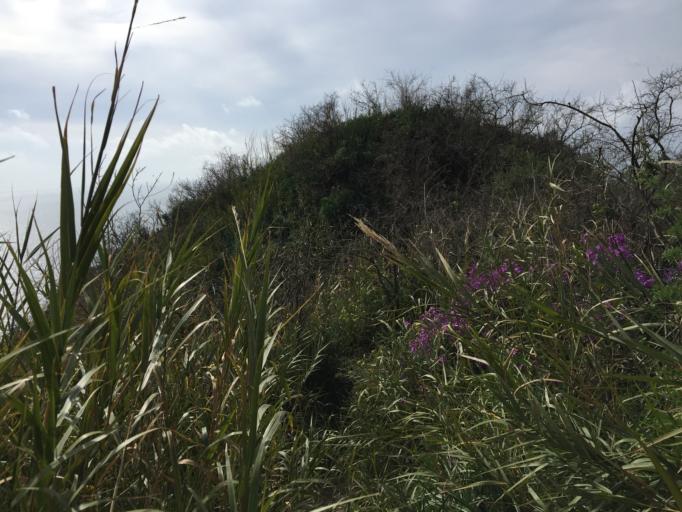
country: IT
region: Campania
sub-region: Provincia di Napoli
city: Bacoli
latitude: 40.7816
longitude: 14.0866
